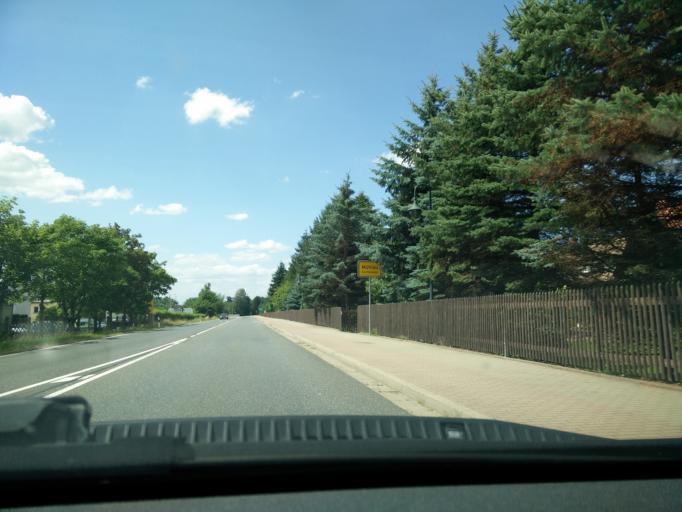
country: DE
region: Saxony
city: Muhlau
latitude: 50.8987
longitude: 12.7719
